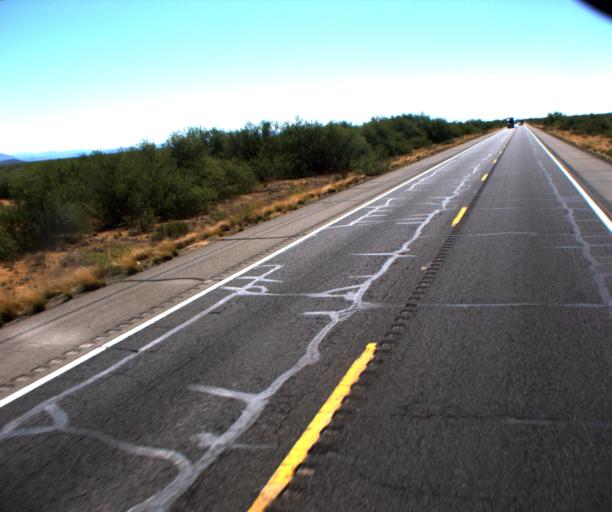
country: US
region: Arizona
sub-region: Yavapai County
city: Congress
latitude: 34.1150
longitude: -112.9384
